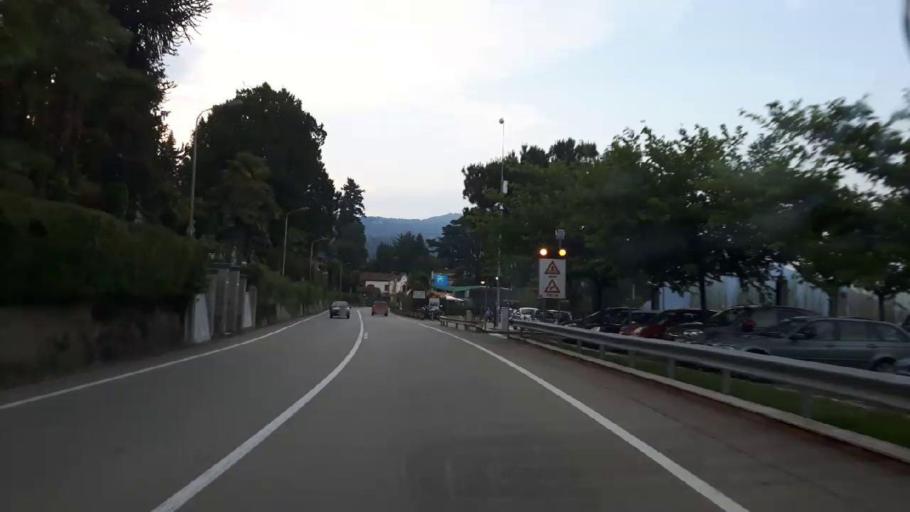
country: IT
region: Piedmont
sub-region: Provincia di Novara
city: Meina
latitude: 45.7859
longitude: 8.5405
